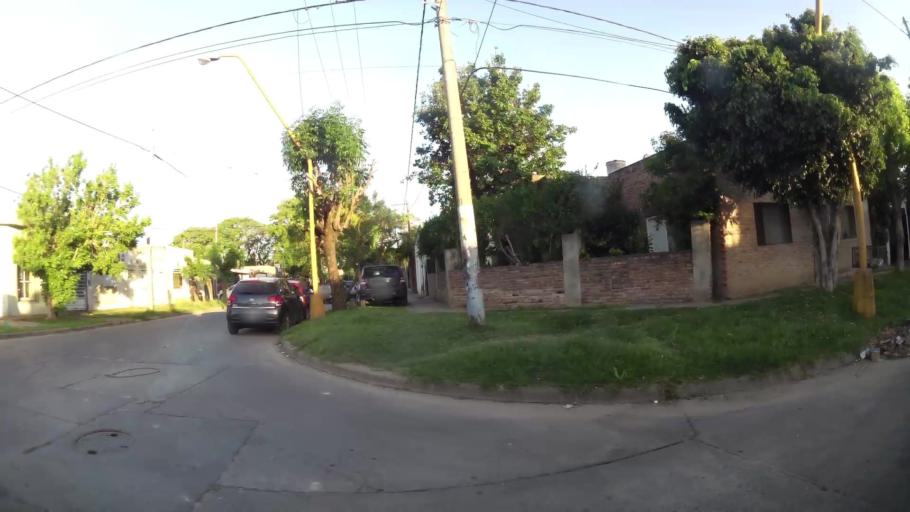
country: AR
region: Santa Fe
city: Santa Fe de la Vera Cruz
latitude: -31.6024
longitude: -60.6863
